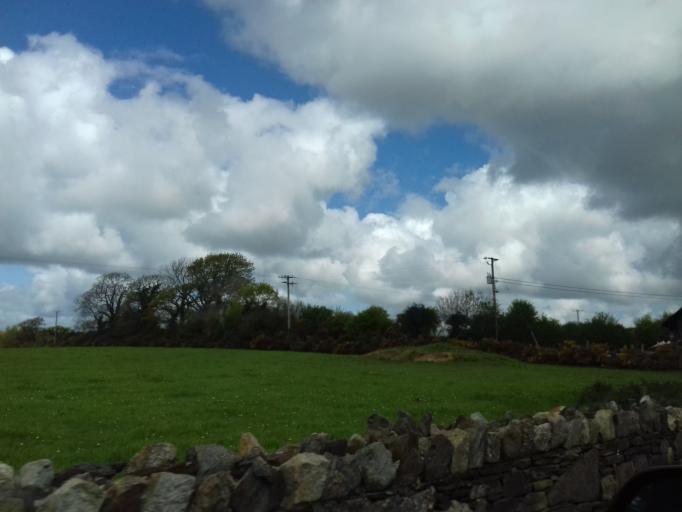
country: IE
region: Leinster
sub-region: Loch Garman
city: Castlebridge
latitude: 52.3799
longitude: -6.5032
